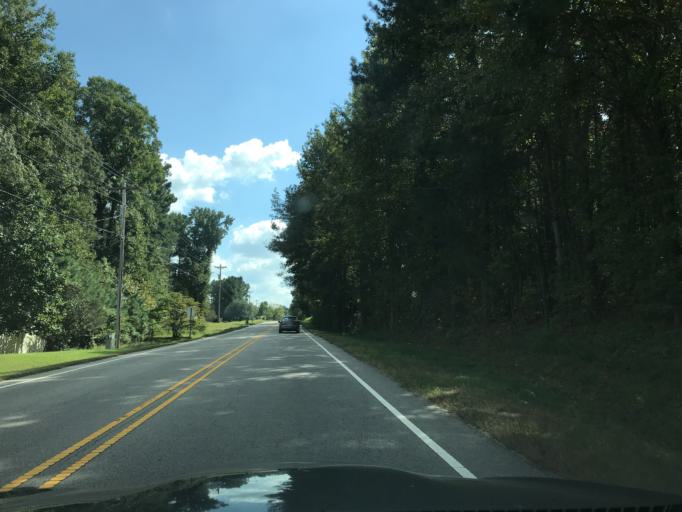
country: US
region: North Carolina
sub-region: Wake County
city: Rolesville
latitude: 35.9020
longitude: -78.5248
